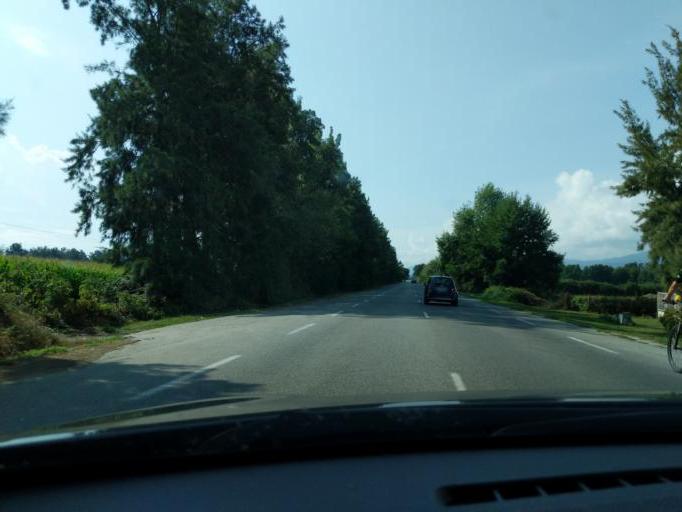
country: FR
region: Corsica
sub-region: Departement de la Haute-Corse
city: Ghisonaccia
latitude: 41.9725
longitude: 9.3988
